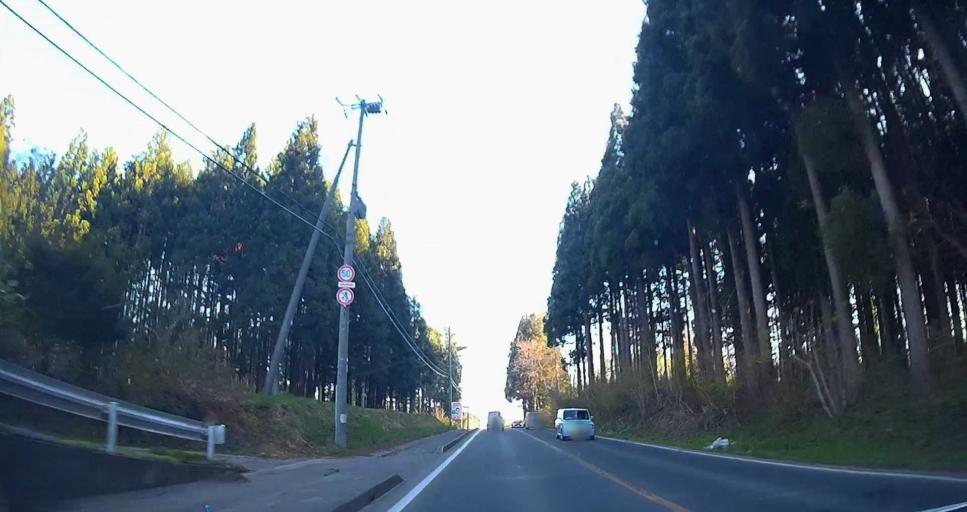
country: JP
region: Aomori
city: Mutsu
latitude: 41.3248
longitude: 141.2170
